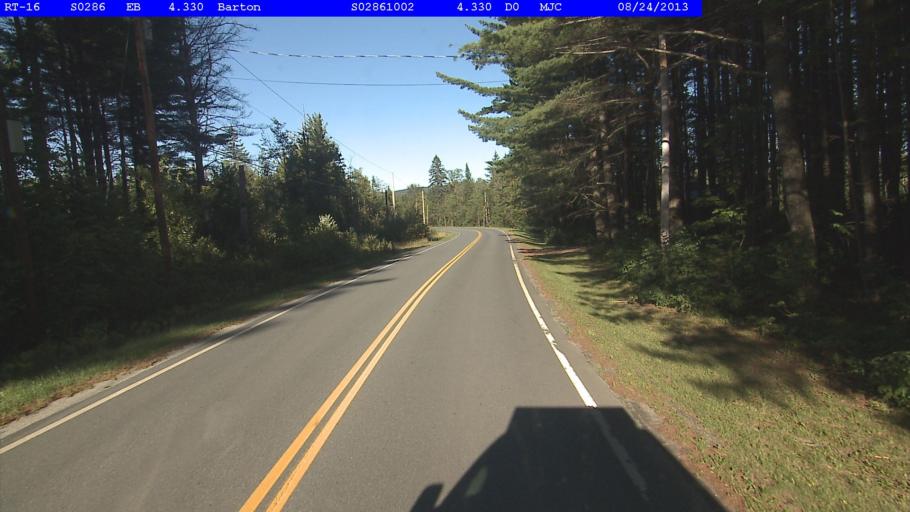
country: US
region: Vermont
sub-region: Orleans County
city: Newport
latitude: 44.7823
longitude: -72.1209
